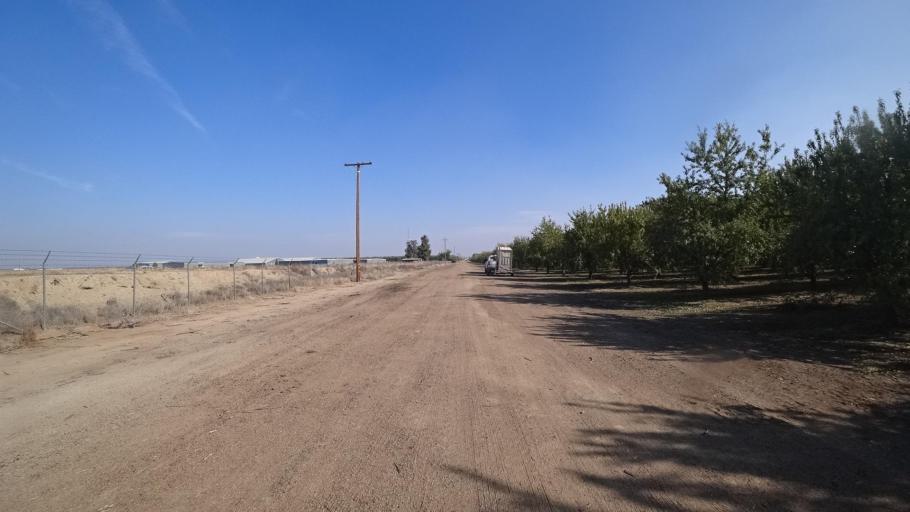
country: US
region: California
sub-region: Kern County
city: McFarland
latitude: 35.6311
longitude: -119.2126
